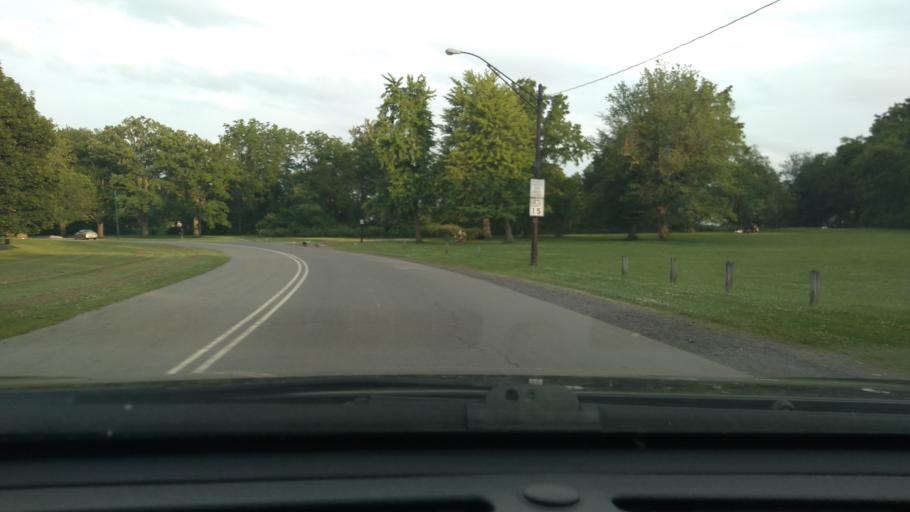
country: US
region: New York
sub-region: Erie County
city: Lackawanna
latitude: 42.8284
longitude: -78.8339
